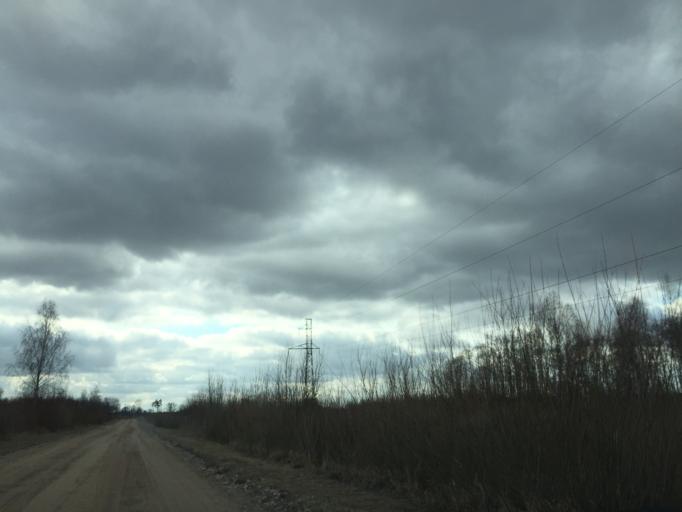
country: LV
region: Vecumnieki
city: Vecumnieki
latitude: 56.5737
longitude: 24.6011
